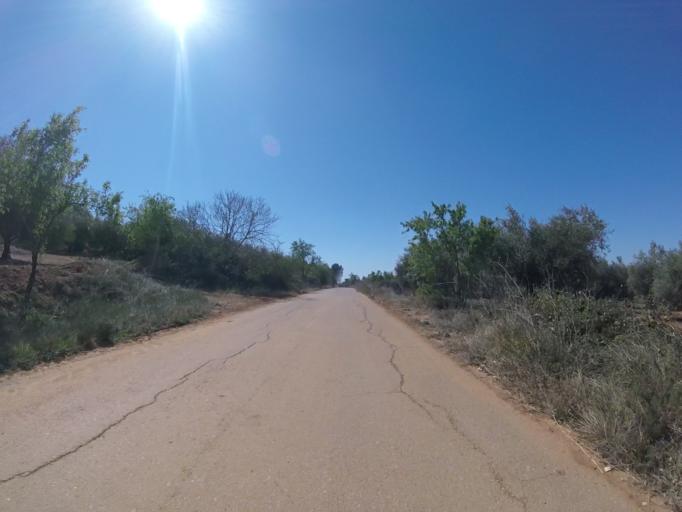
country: ES
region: Valencia
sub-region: Provincia de Castello
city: Cuevas de Vinroma
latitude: 40.3873
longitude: 0.1589
